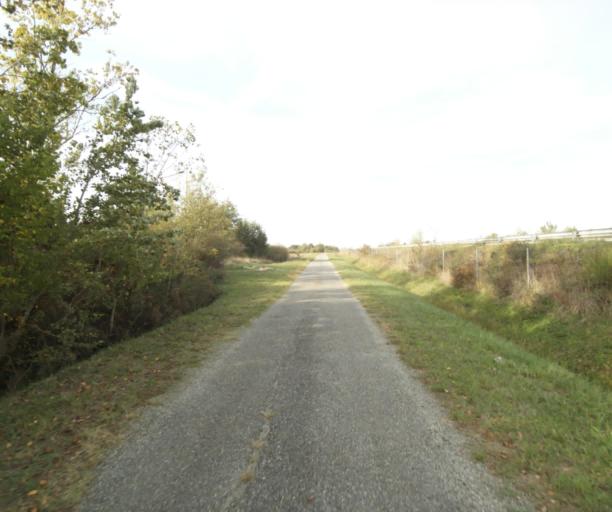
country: FR
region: Midi-Pyrenees
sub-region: Departement du Tarn-et-Garonne
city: Campsas
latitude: 43.8741
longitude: 1.3171
